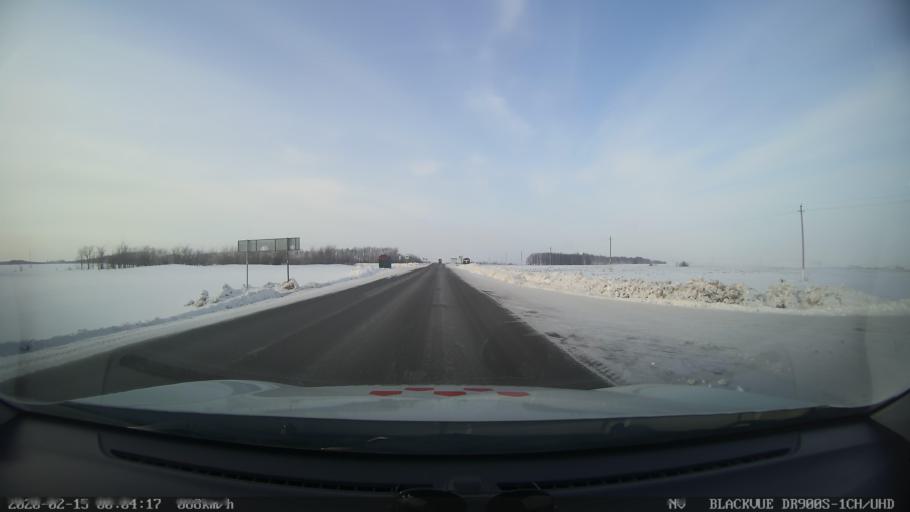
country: RU
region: Tatarstan
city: Kuybyshevskiy Zaton
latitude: 55.3809
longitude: 48.9856
